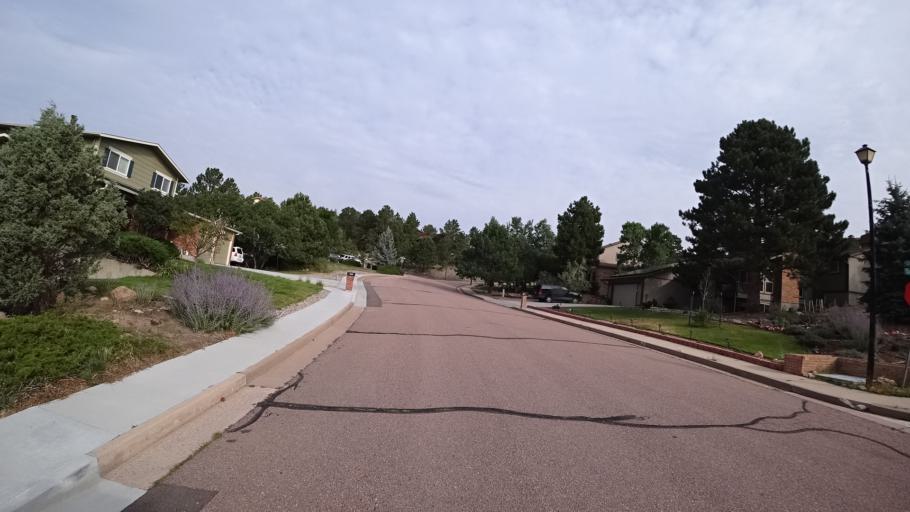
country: US
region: Colorado
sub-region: El Paso County
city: Air Force Academy
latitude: 38.9331
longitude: -104.8445
